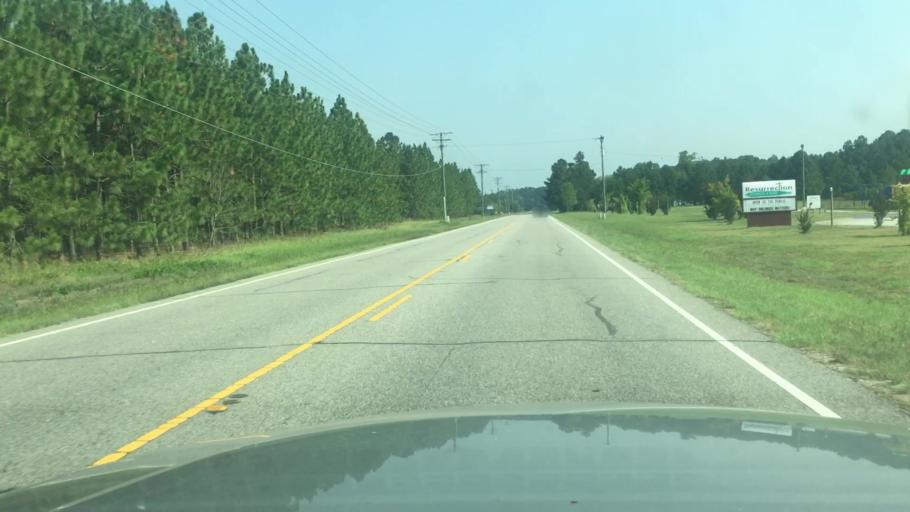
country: US
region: North Carolina
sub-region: Cumberland County
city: Hope Mills
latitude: 34.9053
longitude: -78.9027
